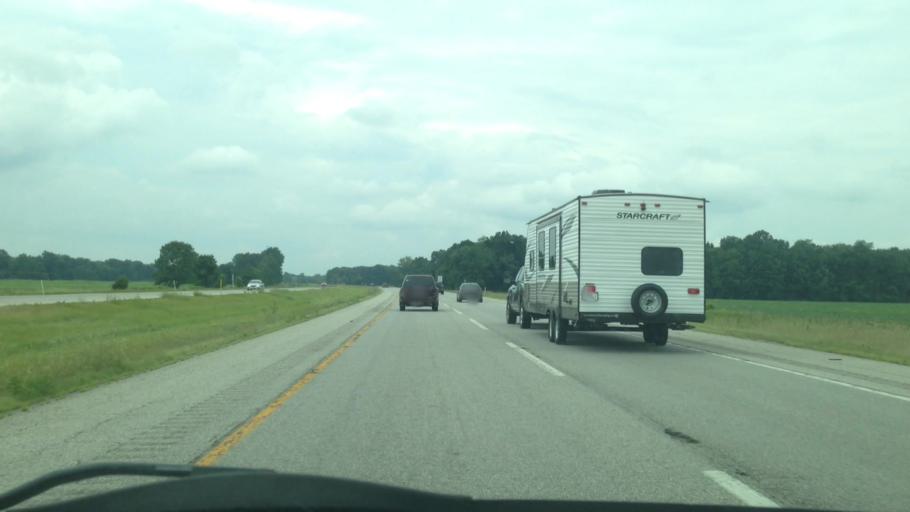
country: US
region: Indiana
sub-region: Elkhart County
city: Middlebury
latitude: 41.7470
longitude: -85.7033
